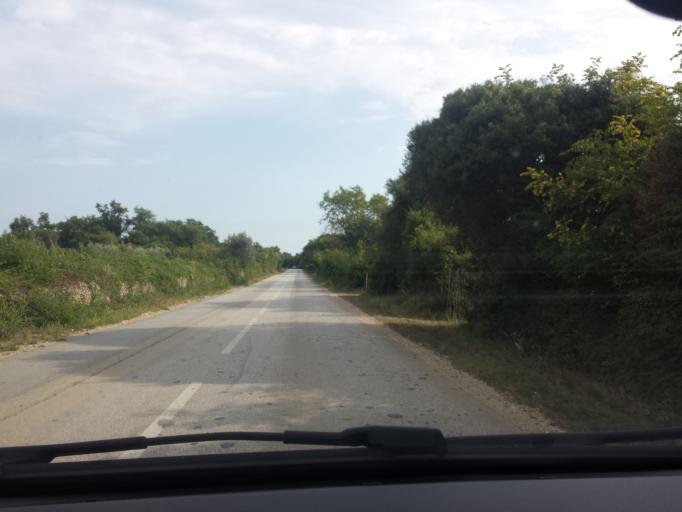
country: HR
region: Istarska
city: Galizana
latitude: 44.9106
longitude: 13.8567
